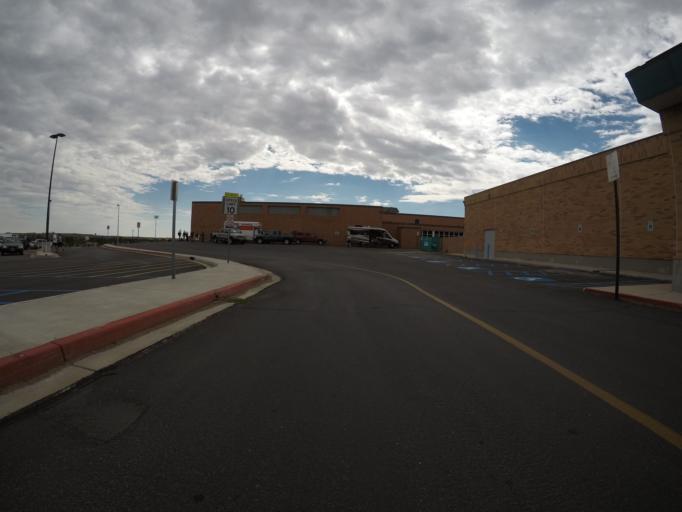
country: US
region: Wyoming
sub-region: Laramie County
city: Fox Farm-College
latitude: 41.1474
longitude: -104.7784
